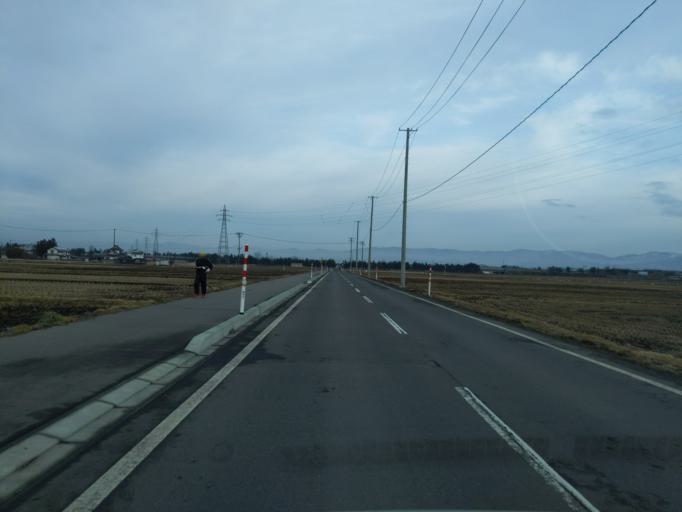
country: JP
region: Iwate
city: Mizusawa
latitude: 39.1372
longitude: 141.1121
